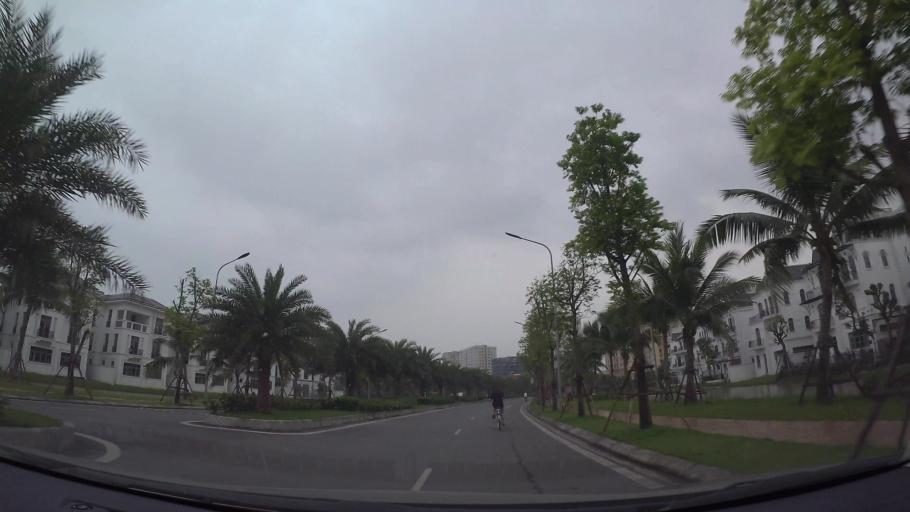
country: VN
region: Ha Noi
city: Trau Quy
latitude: 21.0419
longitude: 105.9080
